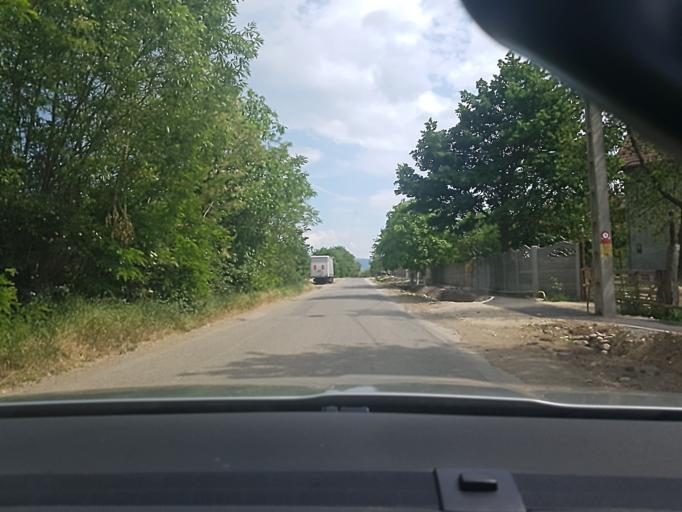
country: RO
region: Hunedoara
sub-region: Comuna Calan
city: Calan
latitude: 45.7231
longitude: 23.0225
